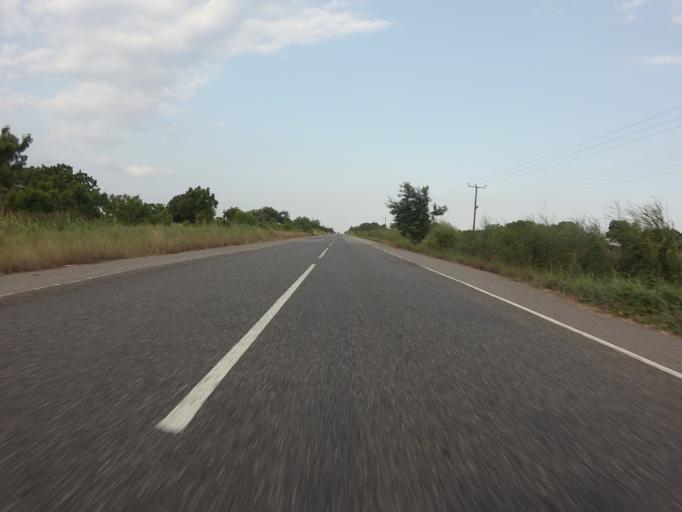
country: GH
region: Volta
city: Anloga
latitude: 6.0863
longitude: 0.5488
